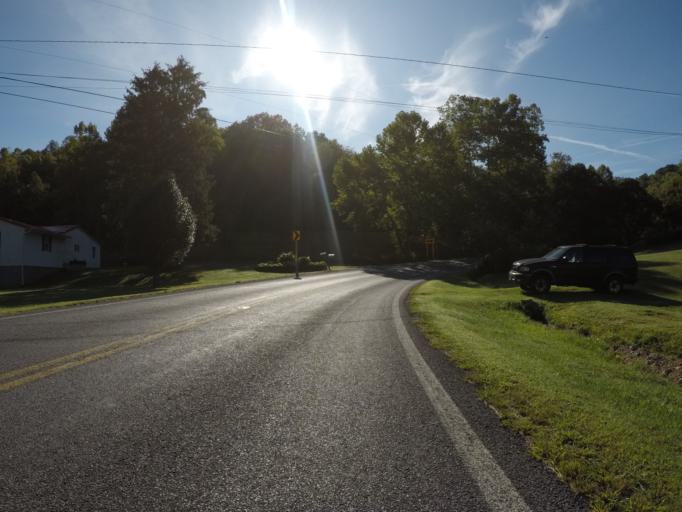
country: US
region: West Virginia
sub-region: Cabell County
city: Huntington
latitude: 38.4956
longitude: -82.4869
